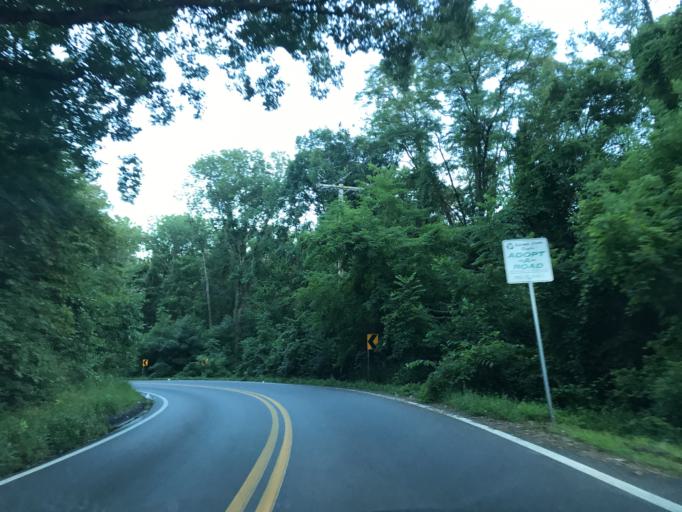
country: US
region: Maryland
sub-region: Baltimore County
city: Woodlawn
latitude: 39.3134
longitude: -76.7249
